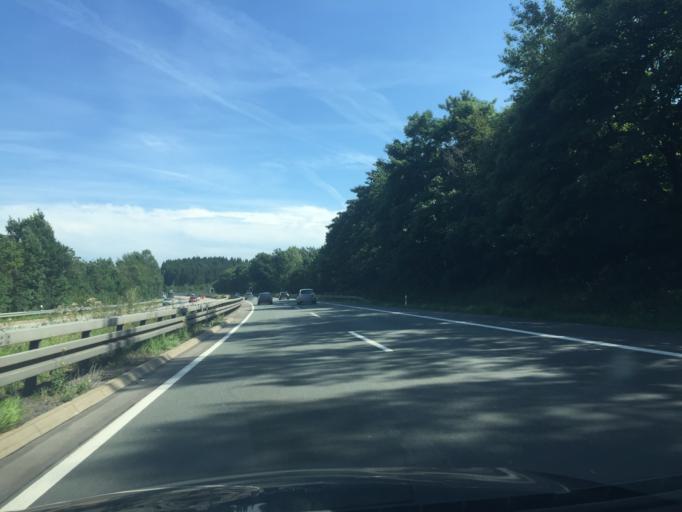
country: DE
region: North Rhine-Westphalia
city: Bergneustadt
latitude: 51.0670
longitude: 7.7033
